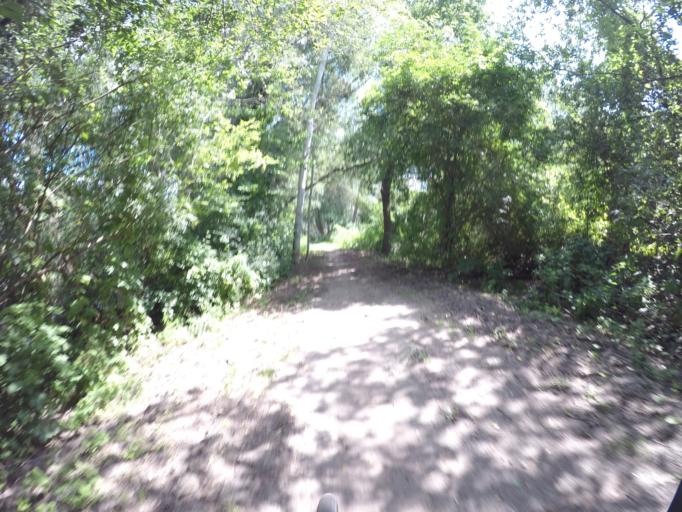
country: DE
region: Brandenburg
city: Stahnsdorf
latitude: 52.3952
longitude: 13.1999
